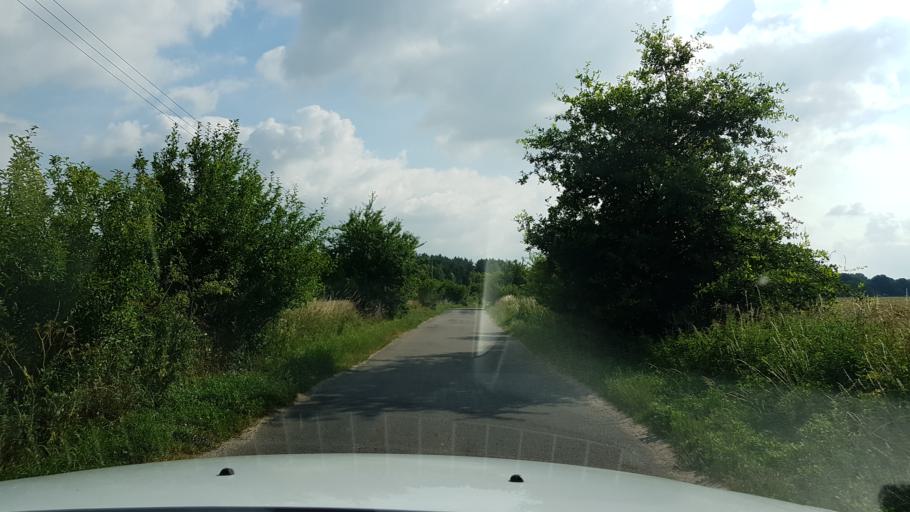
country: PL
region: West Pomeranian Voivodeship
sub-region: Powiat gryfinski
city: Gryfino
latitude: 53.2102
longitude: 14.5859
